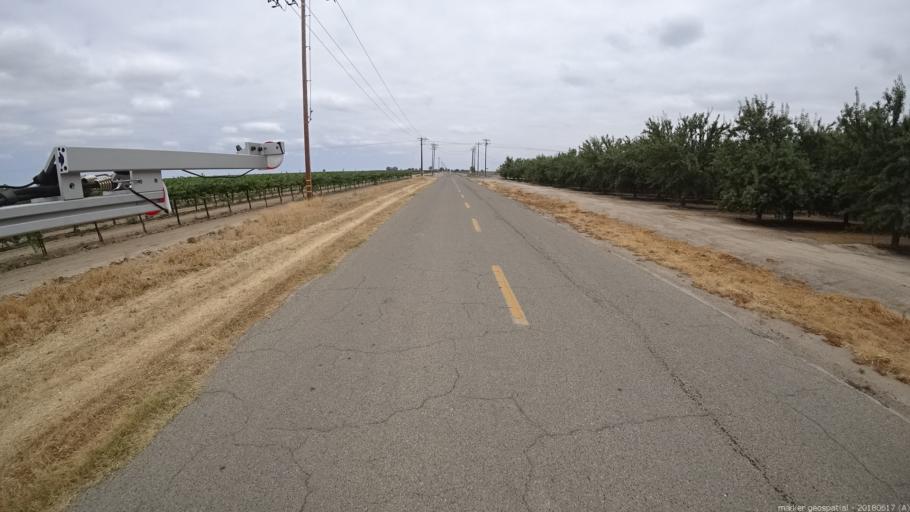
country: US
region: California
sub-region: Madera County
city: Parkwood
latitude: 36.8793
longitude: -120.1650
